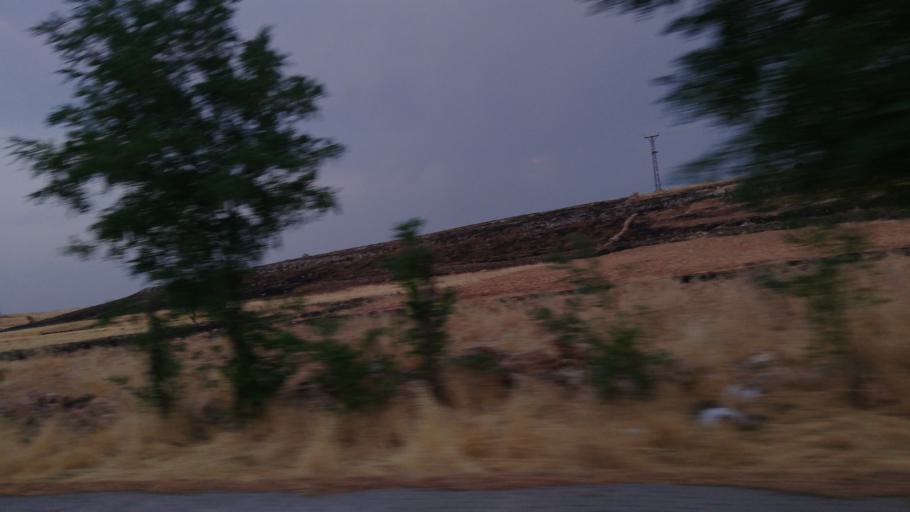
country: TR
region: Mardin
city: Kindirip
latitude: 37.4616
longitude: 41.2256
